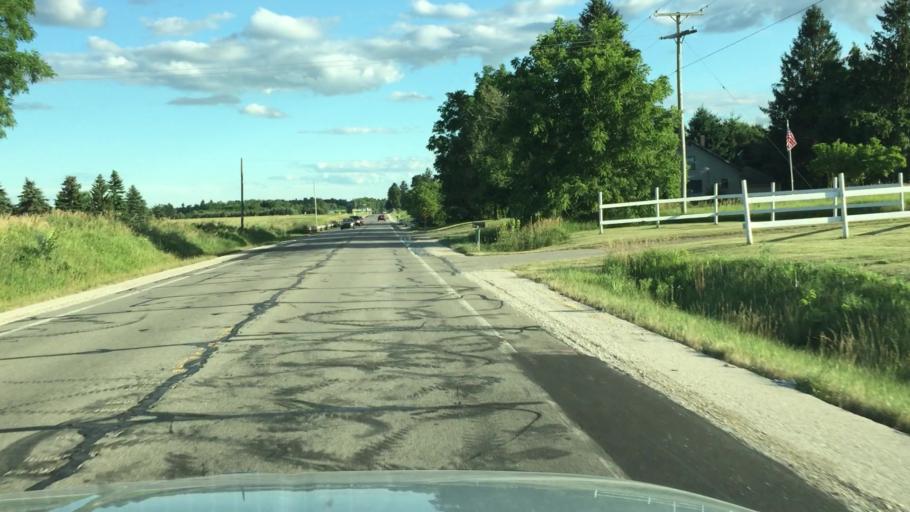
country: US
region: Michigan
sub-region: Saint Clair County
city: Yale
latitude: 43.0818
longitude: -82.7658
